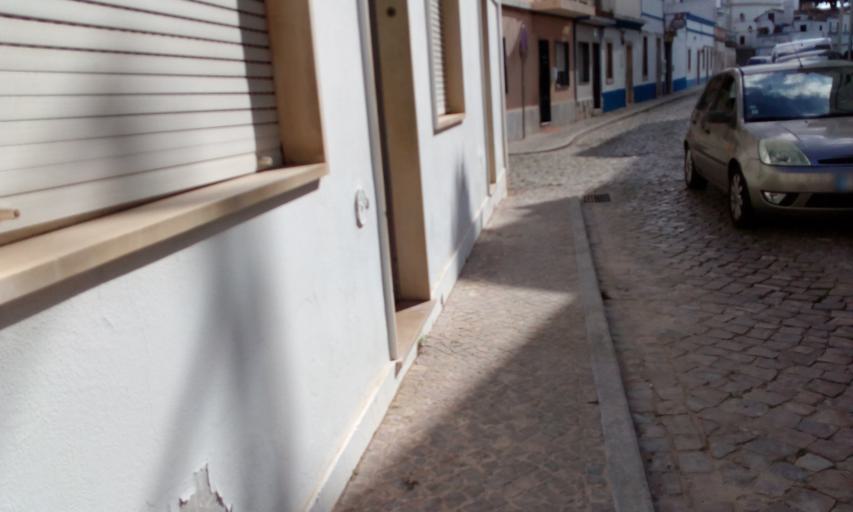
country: PT
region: Faro
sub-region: Loule
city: Loule
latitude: 37.1389
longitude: -8.0241
